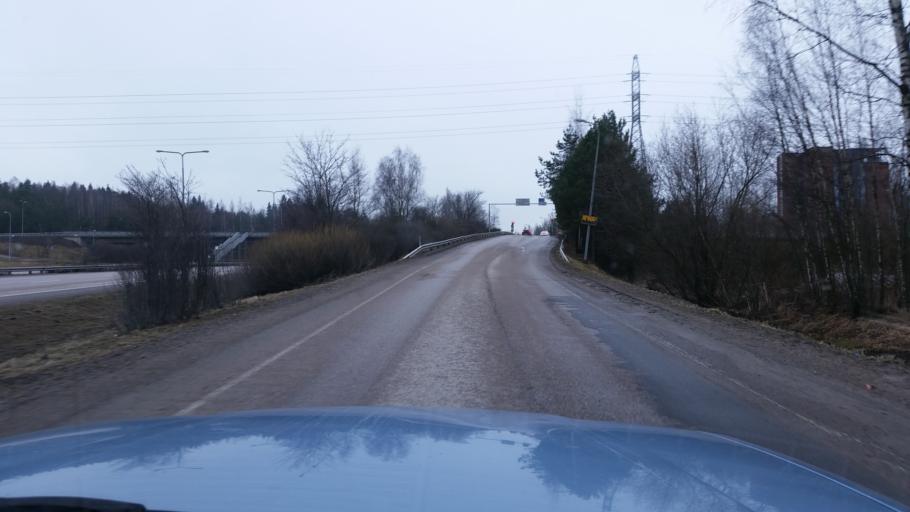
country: FI
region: Uusimaa
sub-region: Helsinki
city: Helsinki
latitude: 60.2215
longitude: 24.9090
